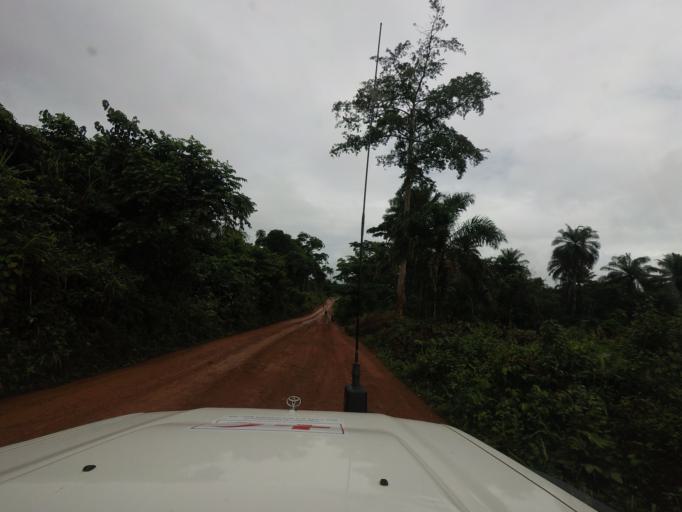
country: GN
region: Nzerekore
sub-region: Nzerekore Prefecture
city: Nzerekore
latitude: 7.7293
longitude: -8.8478
